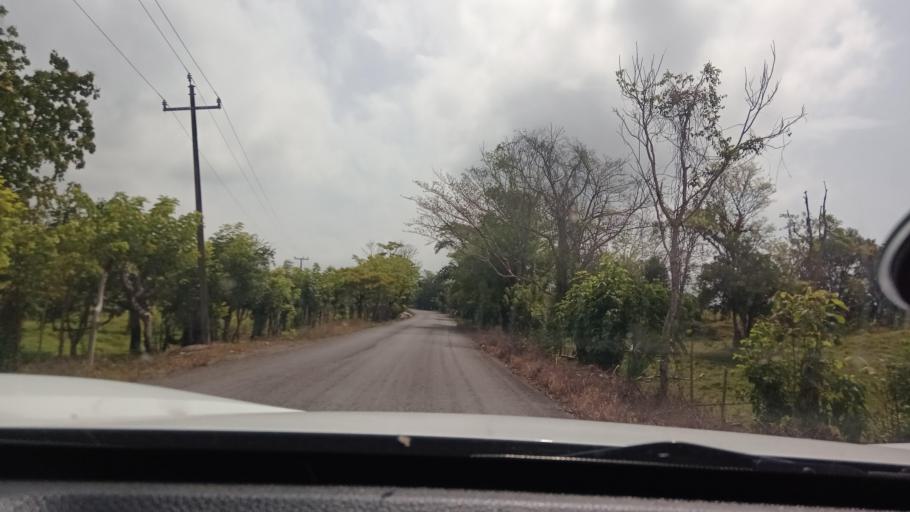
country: MX
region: Tabasco
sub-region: Huimanguillo
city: Francisco Rueda
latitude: 17.5757
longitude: -94.1024
